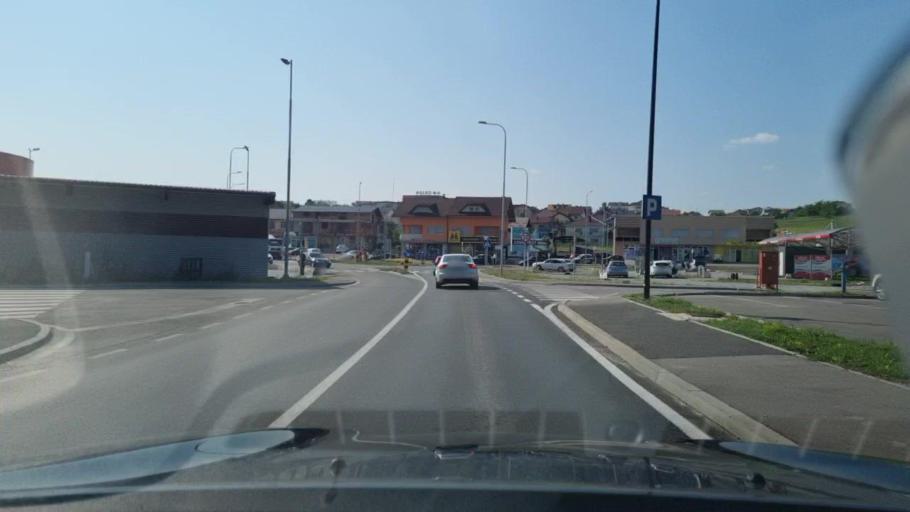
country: BA
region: Federation of Bosnia and Herzegovina
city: Cazin
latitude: 44.9657
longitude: 15.9115
